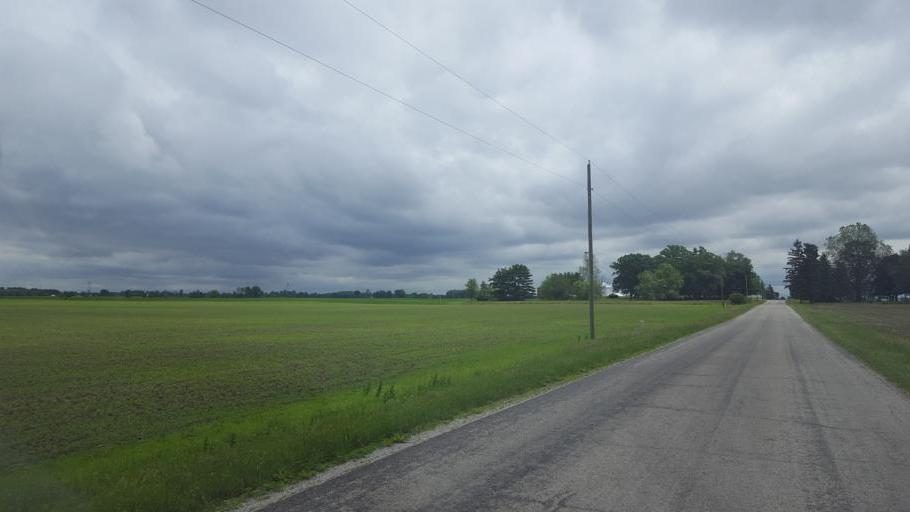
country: US
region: Ohio
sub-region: Crawford County
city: Bucyrus
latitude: 40.7756
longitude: -83.0227
